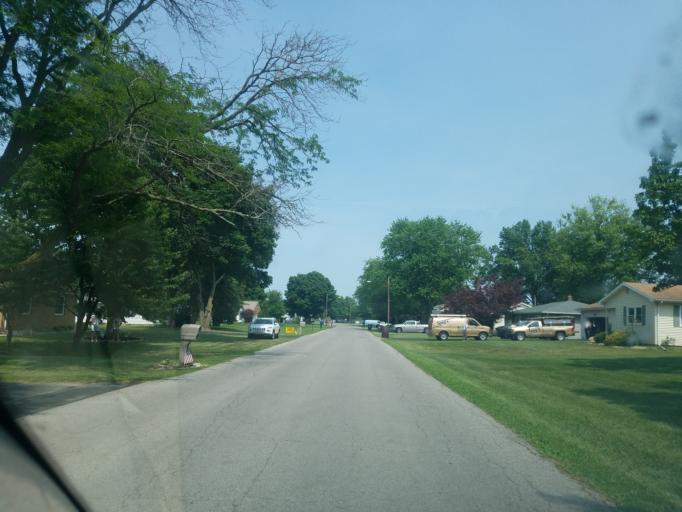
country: US
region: Ohio
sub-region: Seneca County
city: Tiffin
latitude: 41.1148
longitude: -83.2042
